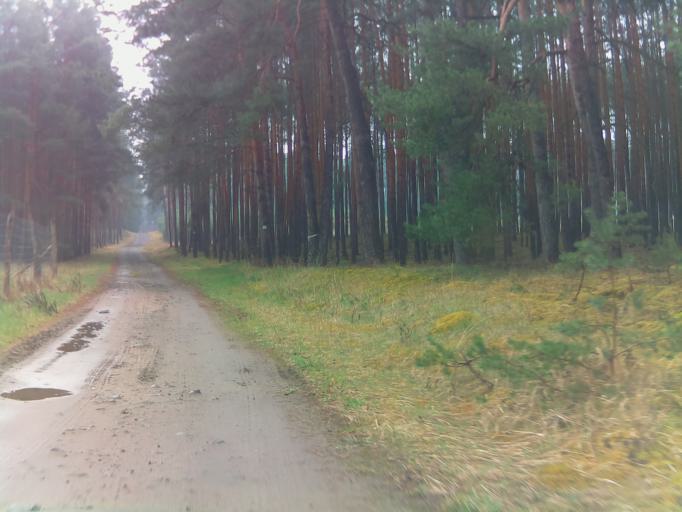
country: DE
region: Brandenburg
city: Friedland
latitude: 52.0303
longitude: 14.2247
